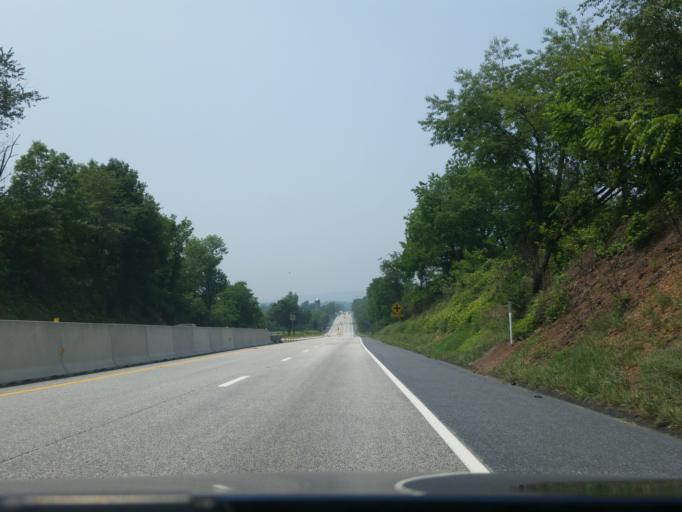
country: US
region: Pennsylvania
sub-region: Lebanon County
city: Jonestown
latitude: 40.4067
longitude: -76.5472
